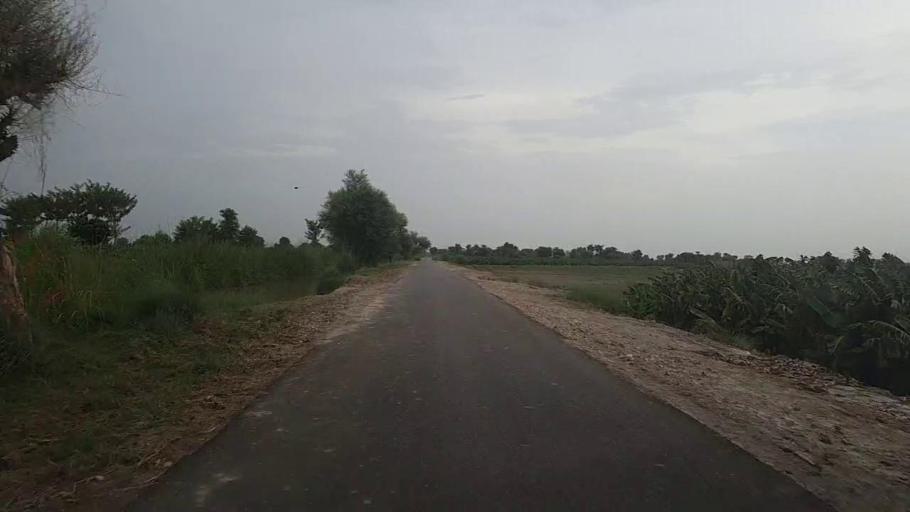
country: PK
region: Sindh
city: Karaundi
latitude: 26.9725
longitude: 68.3609
